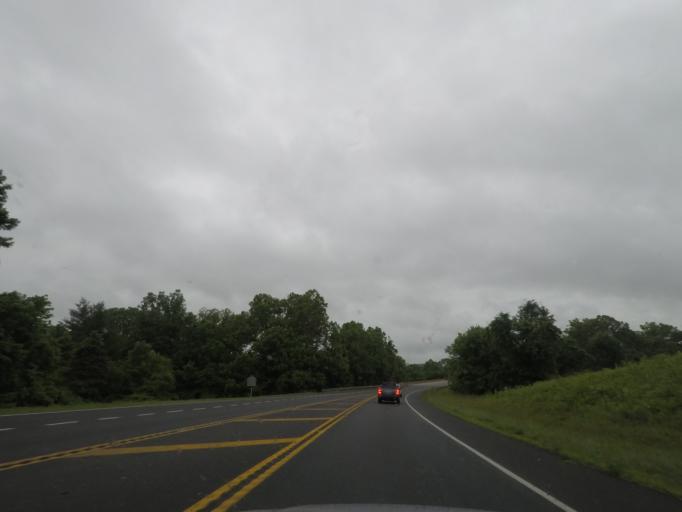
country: US
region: Virginia
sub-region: Orange County
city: Orange
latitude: 38.2796
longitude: -78.1384
